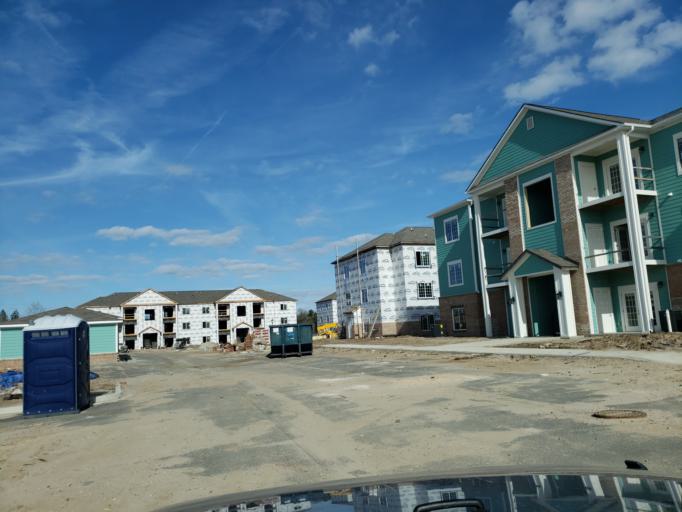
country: US
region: Georgia
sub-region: Chatham County
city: Port Wentworth
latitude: 32.2241
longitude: -81.1884
